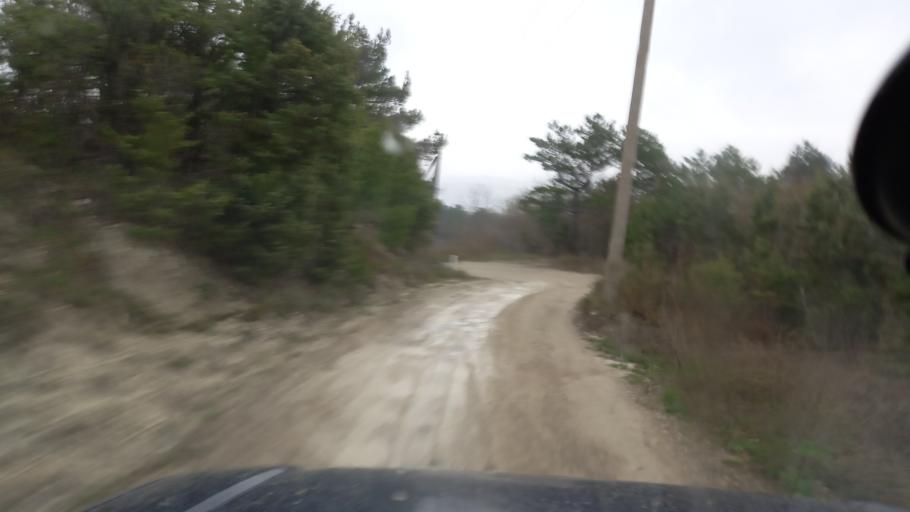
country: RU
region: Krasnodarskiy
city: Dzhubga
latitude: 44.3208
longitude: 38.6804
